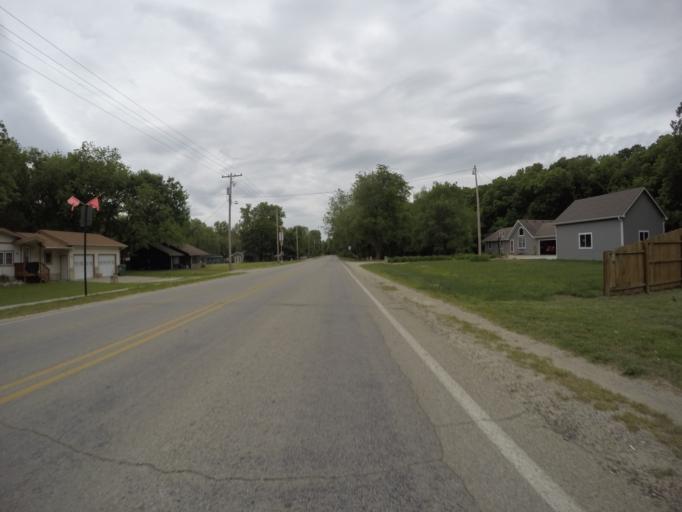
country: US
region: Kansas
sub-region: Pottawatomie County
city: Wamego
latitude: 39.1944
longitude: -96.4268
